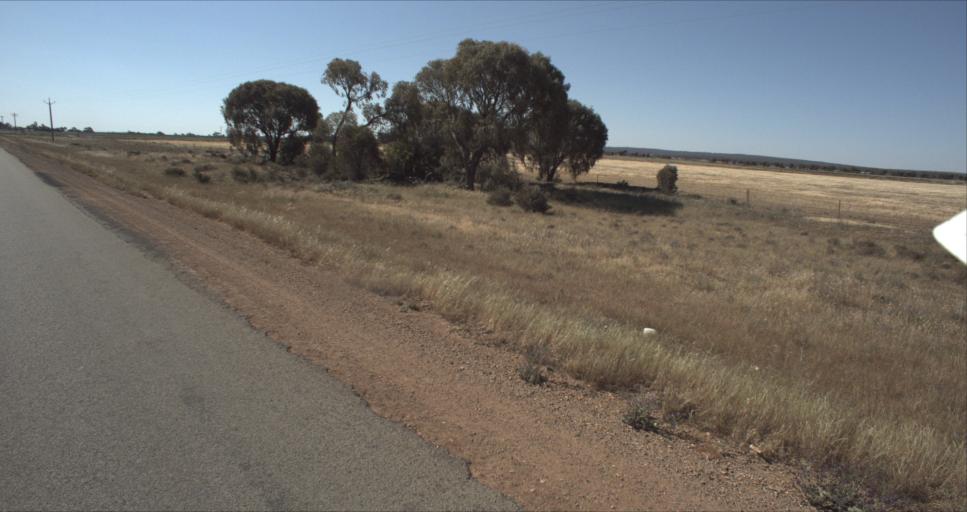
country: AU
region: New South Wales
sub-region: Leeton
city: Leeton
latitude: -34.4890
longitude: 146.3808
